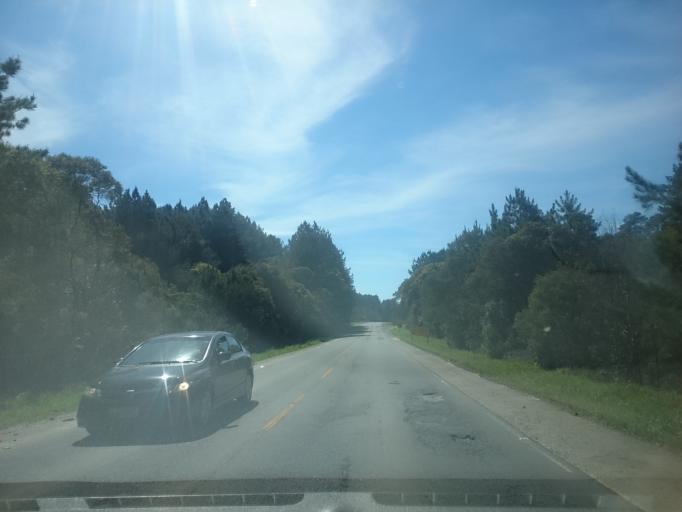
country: BR
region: Santa Catarina
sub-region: Otacilio Costa
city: Otacilio Costa
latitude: -27.7420
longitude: -49.8053
